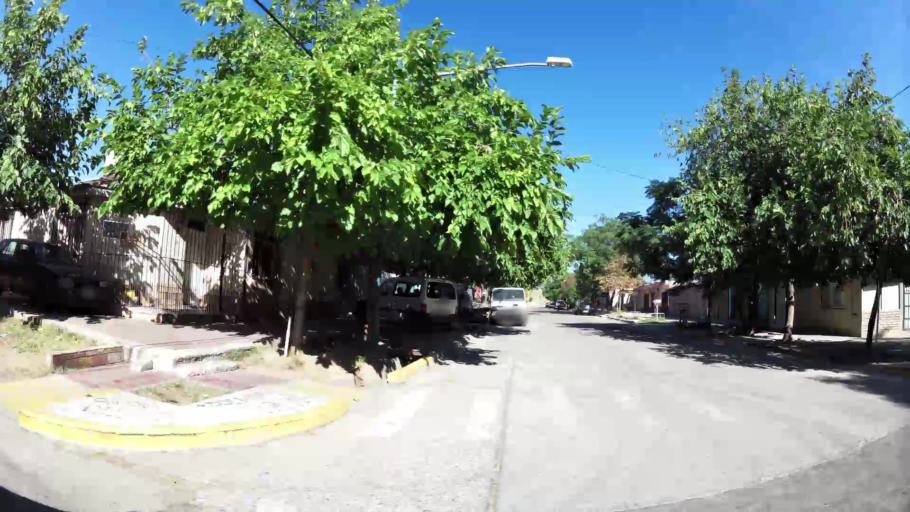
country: AR
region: Mendoza
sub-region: Departamento de Godoy Cruz
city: Godoy Cruz
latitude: -32.9295
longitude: -68.8625
